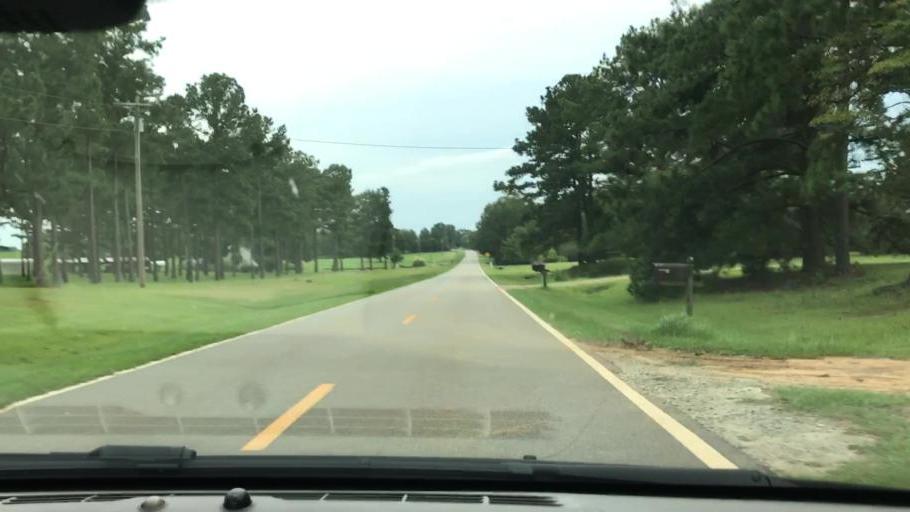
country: US
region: Georgia
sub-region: Early County
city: Blakely
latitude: 31.4405
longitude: -84.9157
